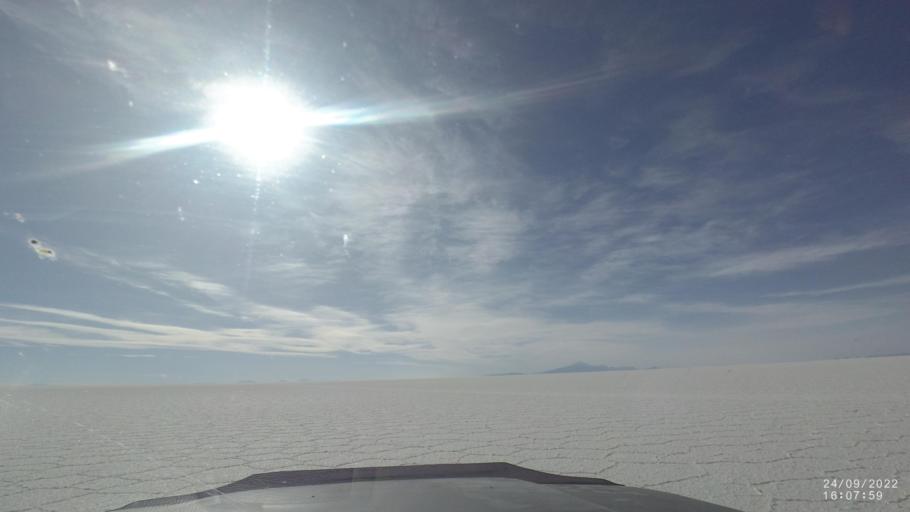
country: BO
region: Potosi
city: Colchani
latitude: -20.2960
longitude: -67.3074
